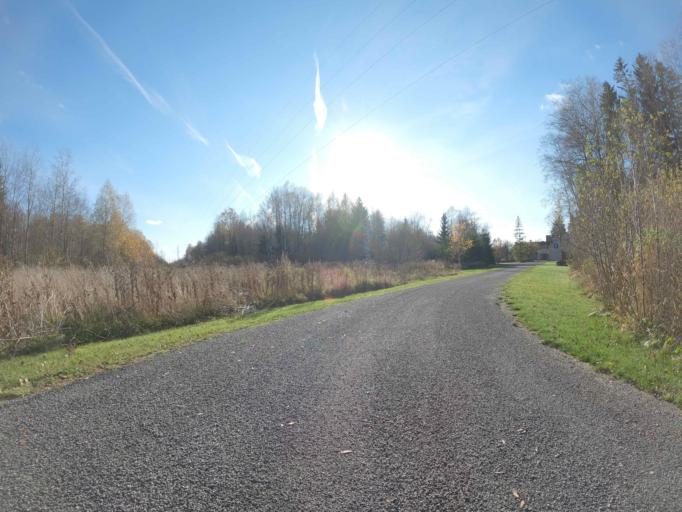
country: EE
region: Raplamaa
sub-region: Rapla vald
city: Rapla
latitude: 59.0055
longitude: 24.8090
